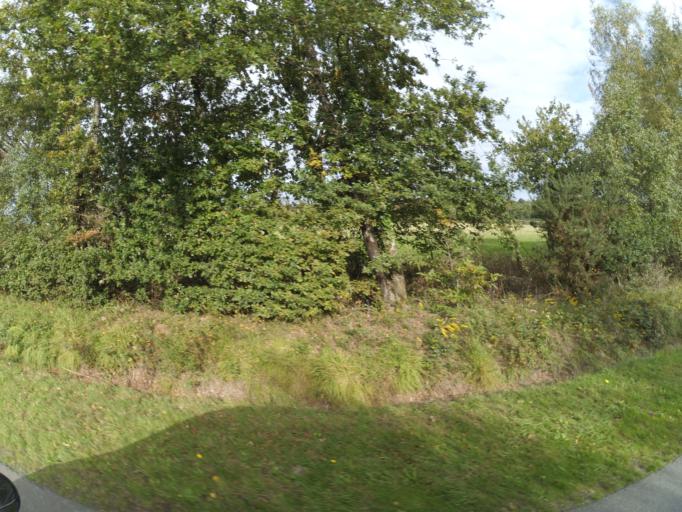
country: FR
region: Pays de la Loire
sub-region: Departement de la Loire-Atlantique
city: Guenrouet
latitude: 47.5554
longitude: -1.9558
